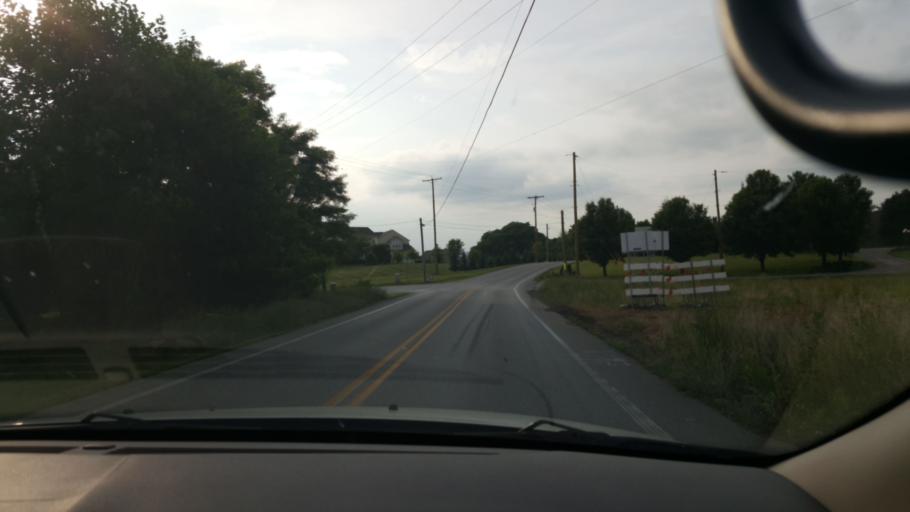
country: US
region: Pennsylvania
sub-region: York County
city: Shiloh
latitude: 39.9916
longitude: -76.7919
